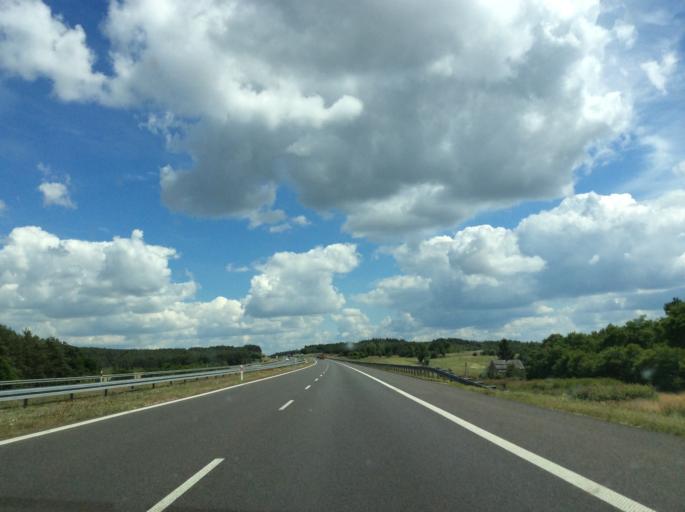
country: PL
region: Greater Poland Voivodeship
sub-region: Powiat kolski
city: Koscielec
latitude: 52.1423
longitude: 18.5293
